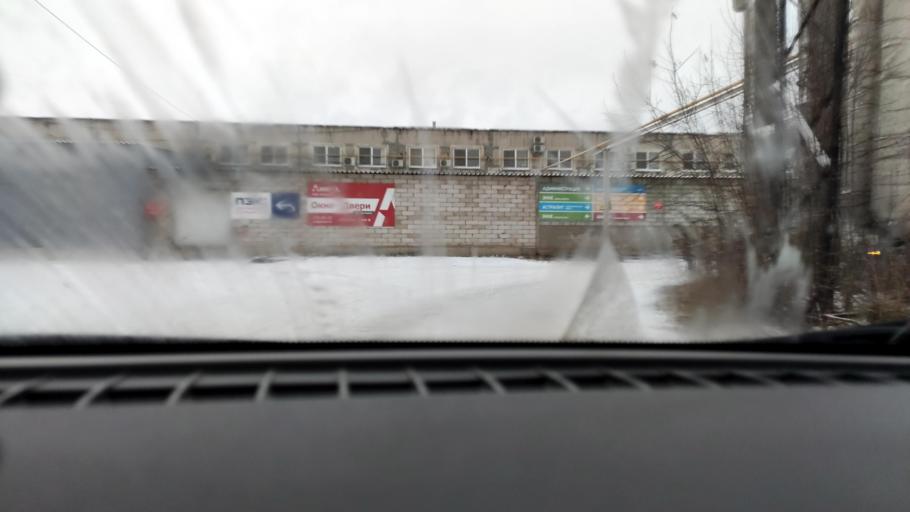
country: RU
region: Perm
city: Kondratovo
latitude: 57.9240
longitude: 56.1667
